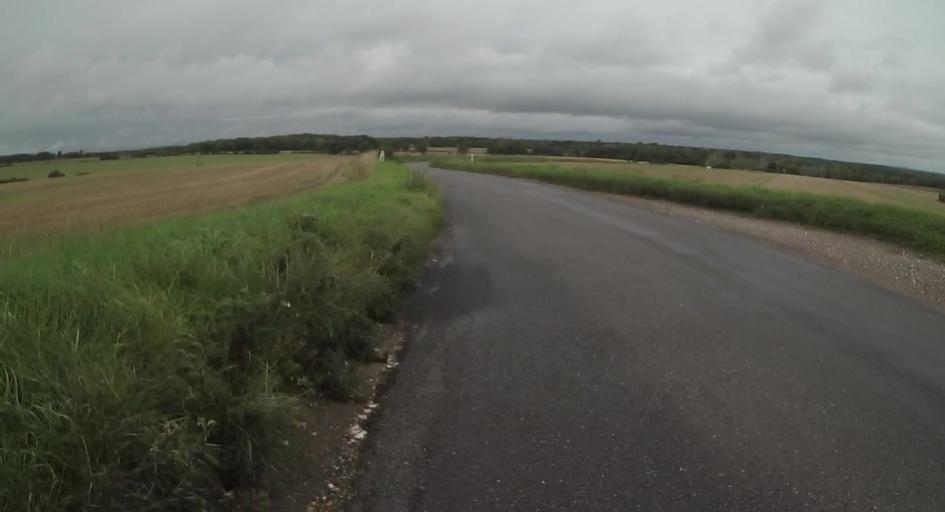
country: GB
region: England
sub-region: Hampshire
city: Tadley
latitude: 51.2968
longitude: -1.1525
